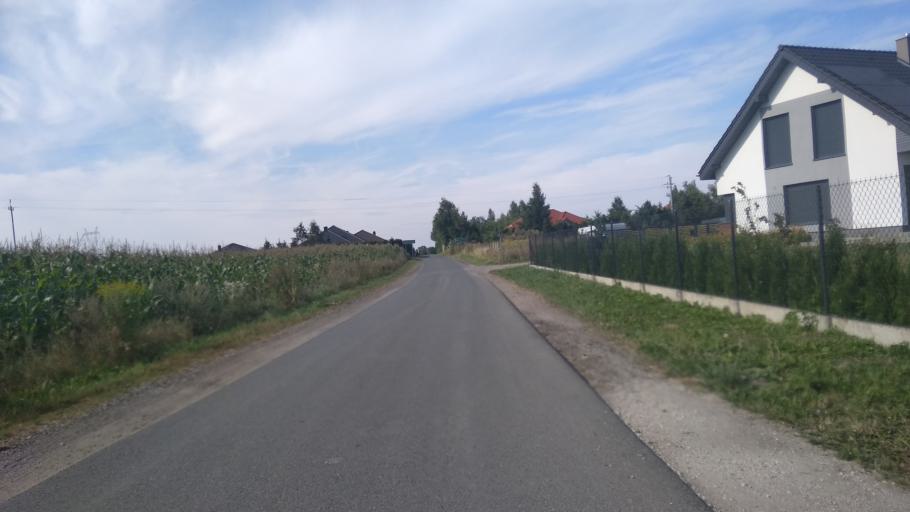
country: PL
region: Kujawsko-Pomorskie
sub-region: Powiat bydgoski
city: Osielsko
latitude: 53.2174
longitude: 18.1475
